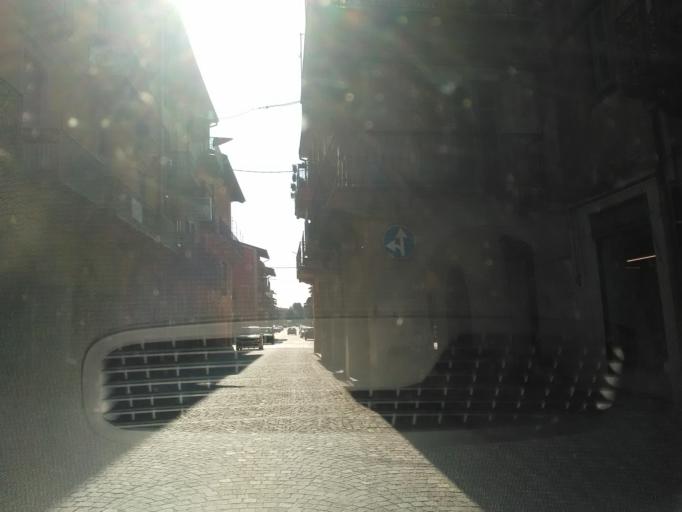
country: IT
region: Piedmont
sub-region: Provincia di Vercelli
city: Gattinara
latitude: 45.6137
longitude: 8.3715
